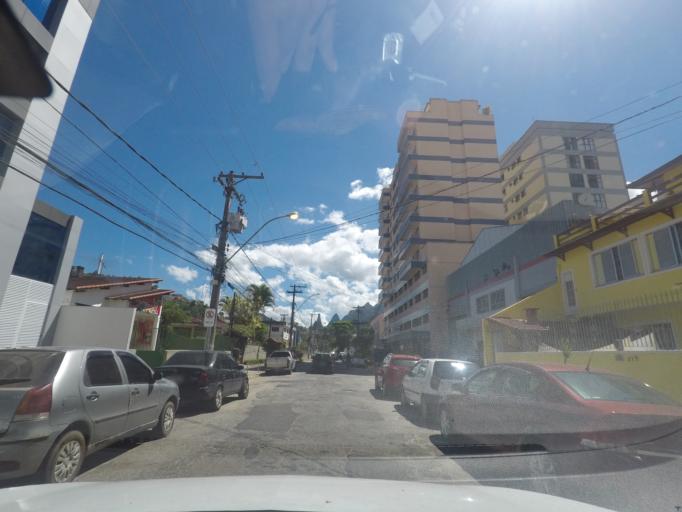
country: BR
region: Rio de Janeiro
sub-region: Teresopolis
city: Teresopolis
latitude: -22.4179
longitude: -42.9719
